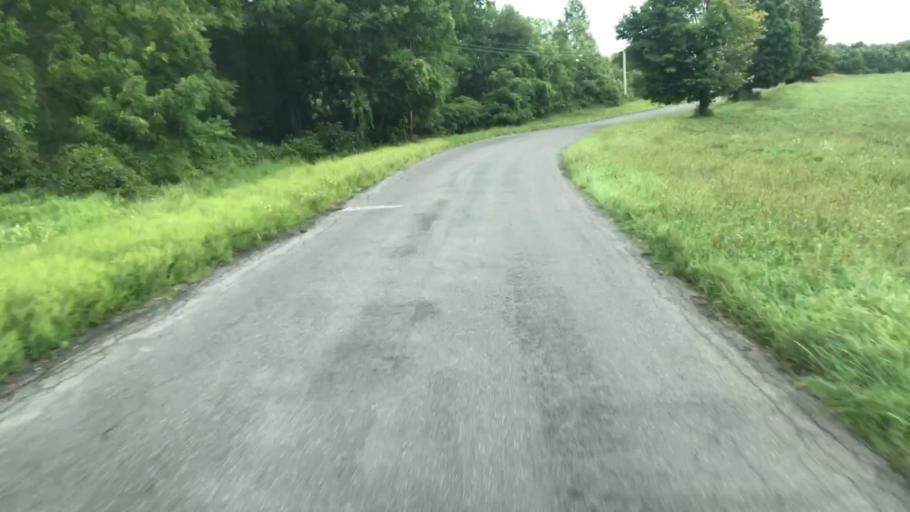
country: US
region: New York
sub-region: Onondaga County
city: Skaneateles
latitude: 42.9828
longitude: -76.4536
